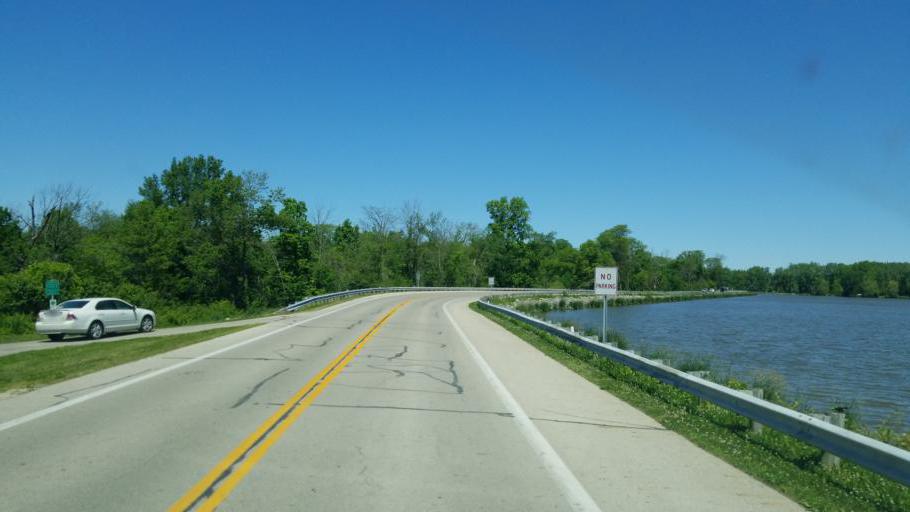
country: US
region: Ohio
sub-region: Shelby County
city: Fort Loramie
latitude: 40.3614
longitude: -84.3618
